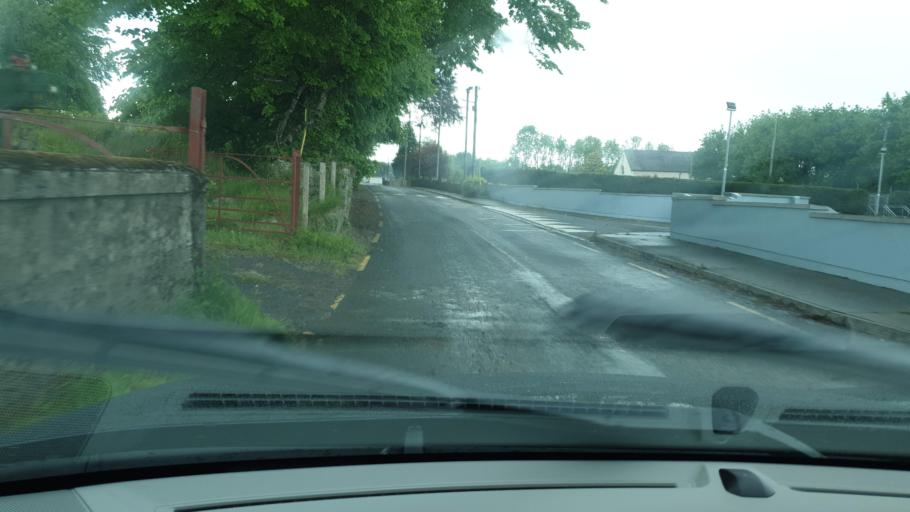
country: IE
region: Leinster
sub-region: Laois
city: Mountrath
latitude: 53.0557
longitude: -7.4076
